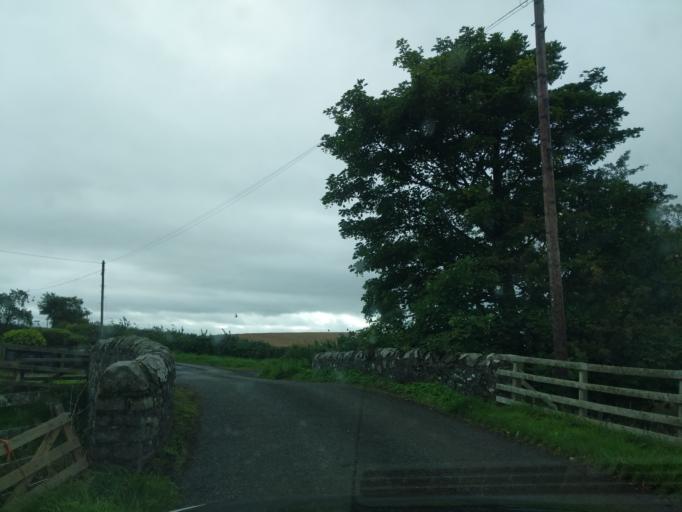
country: GB
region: Scotland
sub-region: The Scottish Borders
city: Saint Boswells
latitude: 55.5887
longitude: -2.6066
